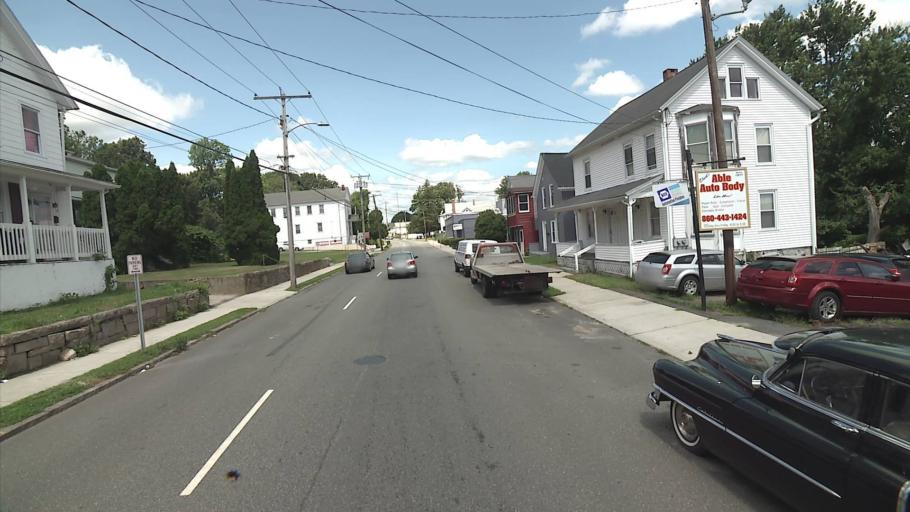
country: US
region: Connecticut
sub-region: New London County
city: New London
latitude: 41.3507
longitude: -72.1082
